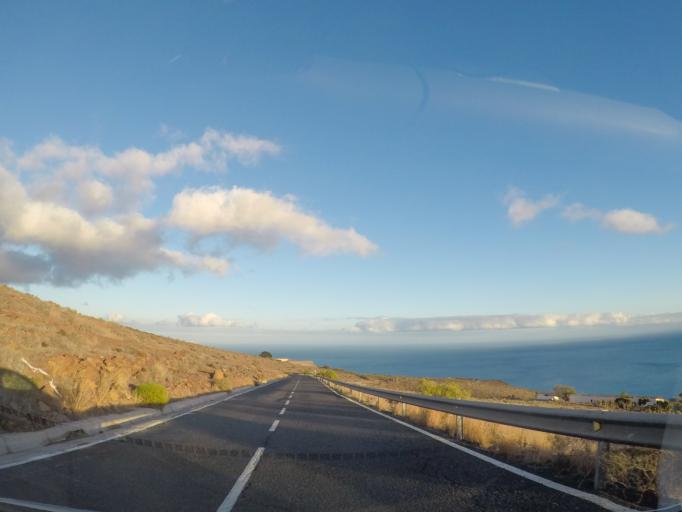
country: ES
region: Canary Islands
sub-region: Provincia de Santa Cruz de Tenerife
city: Alajero
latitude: 28.0396
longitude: -17.2294
